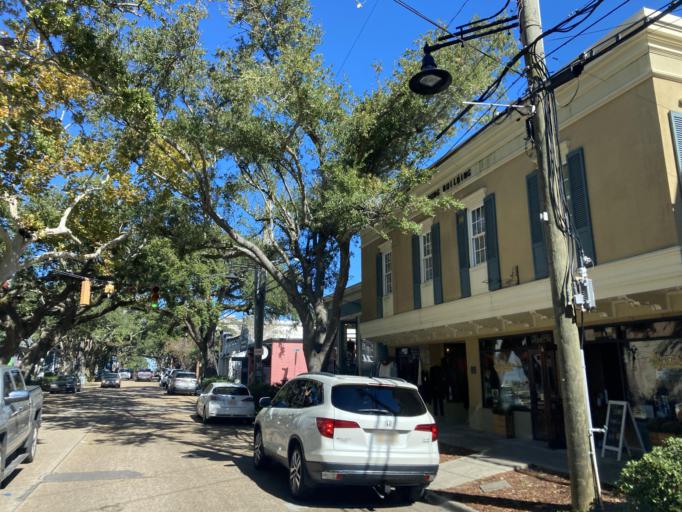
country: US
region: Mississippi
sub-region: Jackson County
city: Ocean Springs
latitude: 30.4125
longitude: -88.8277
